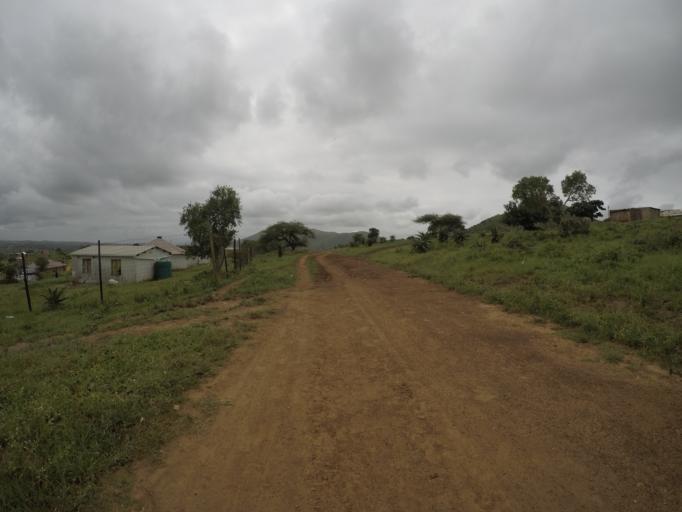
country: ZA
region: KwaZulu-Natal
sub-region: uThungulu District Municipality
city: Empangeni
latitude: -28.5992
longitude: 31.8488
